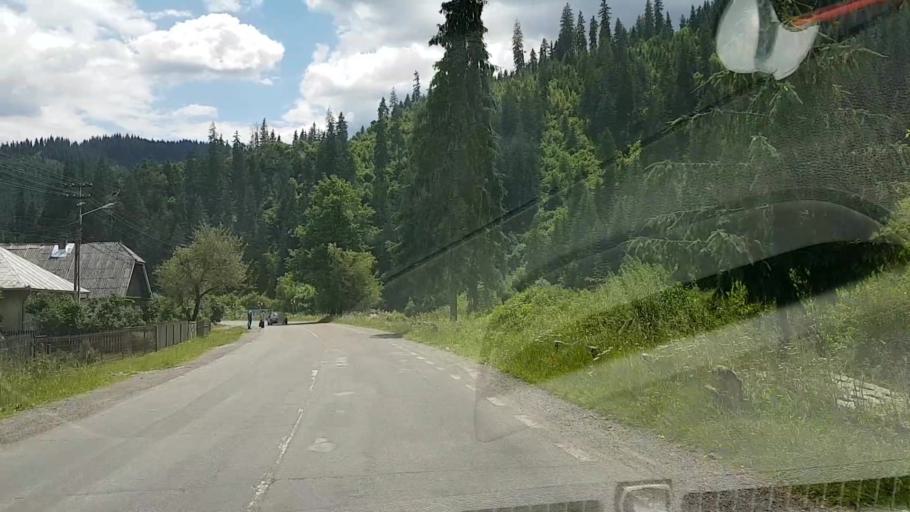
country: RO
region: Suceava
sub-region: Comuna Brosteni
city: Brosteni
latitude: 47.2398
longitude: 25.6912
